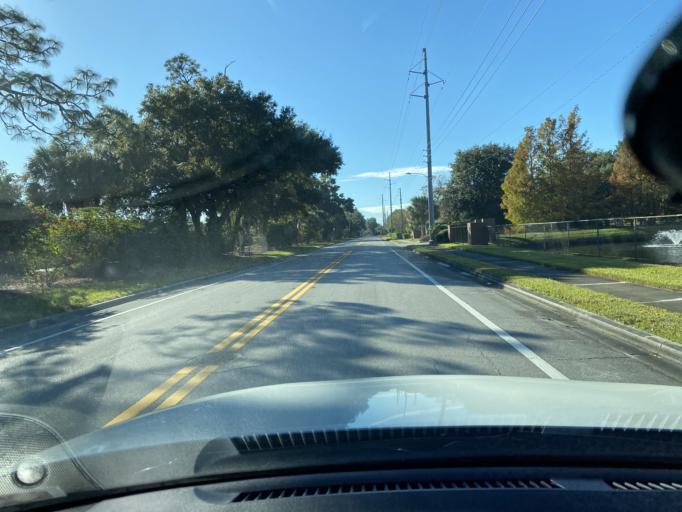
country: US
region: Florida
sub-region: Orange County
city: Azalea Park
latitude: 28.5161
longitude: -81.3021
